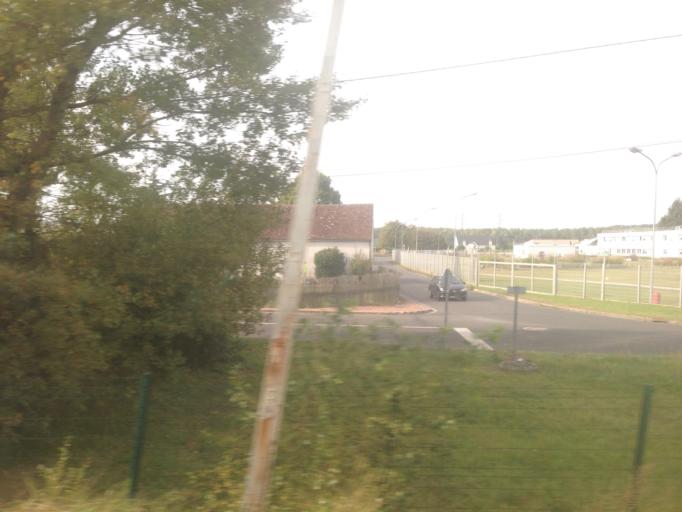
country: FR
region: Centre
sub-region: Departement d'Indre-et-Loire
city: Amboise
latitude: 47.4247
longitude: 0.9885
